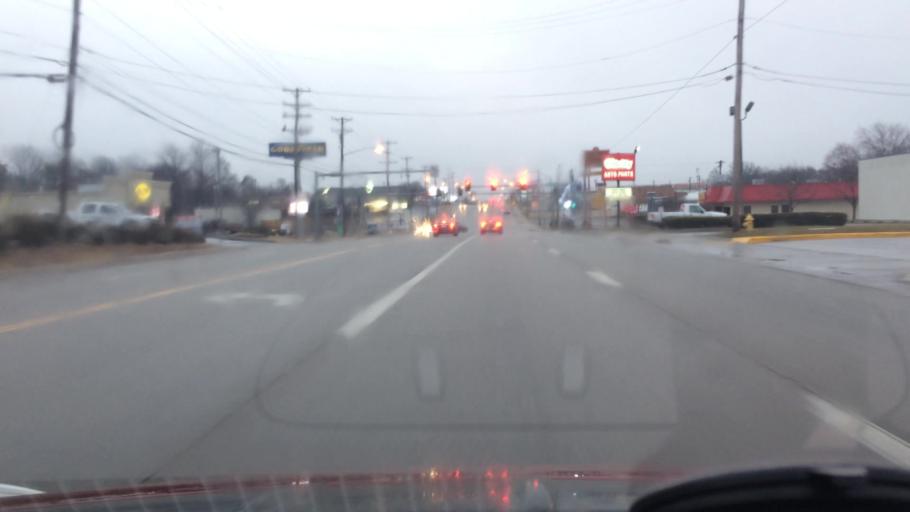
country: US
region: Missouri
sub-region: Greene County
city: Springfield
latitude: 37.1805
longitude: -93.2347
